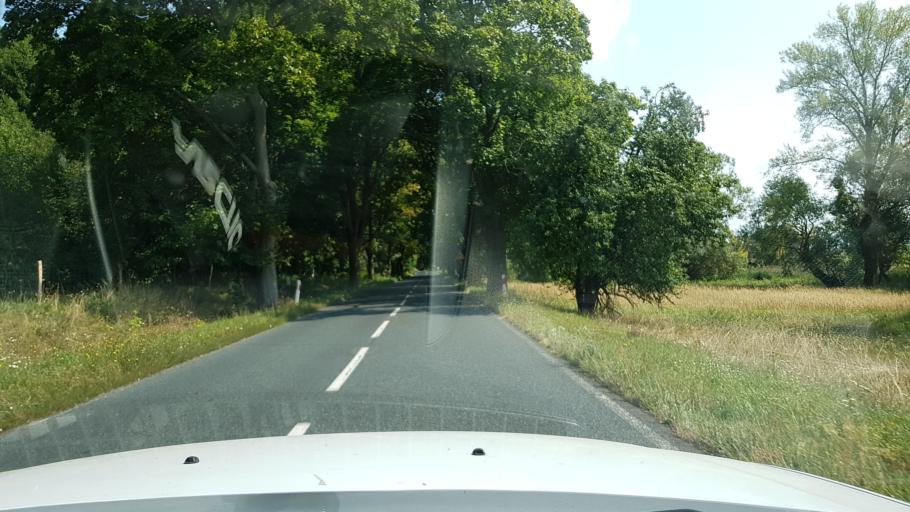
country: PL
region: West Pomeranian Voivodeship
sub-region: Powiat gryfinski
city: Cedynia
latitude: 52.8327
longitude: 14.2069
